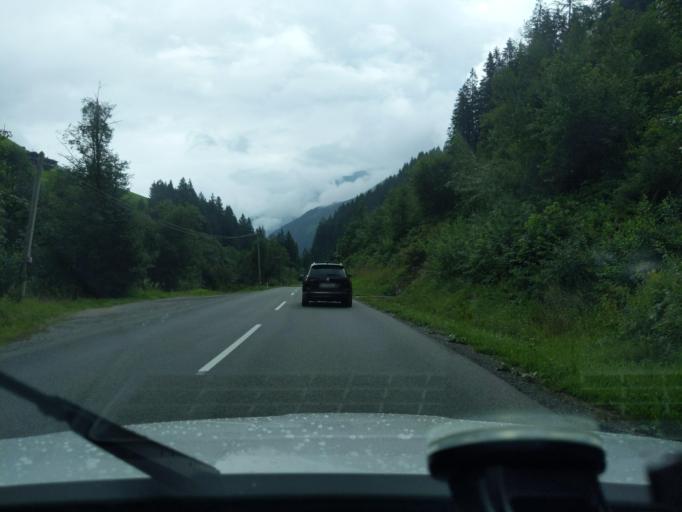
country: AT
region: Tyrol
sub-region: Politischer Bezirk Schwaz
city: Mayrhofen
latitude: 47.1570
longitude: 11.7649
